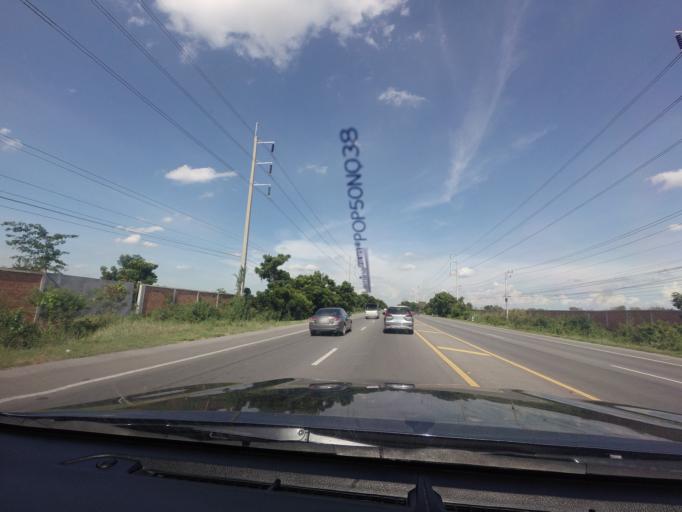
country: TH
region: Suphan Buri
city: Song Phi Nong
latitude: 14.1580
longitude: 100.1350
